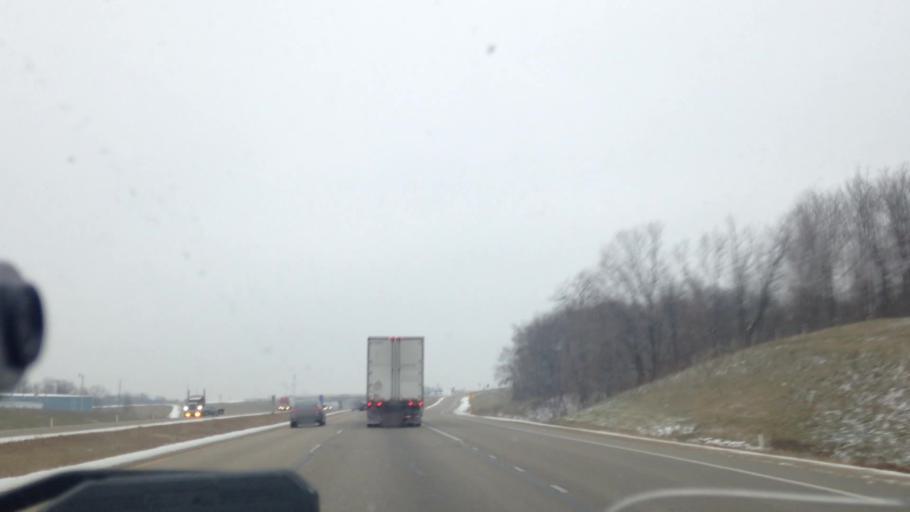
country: US
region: Wisconsin
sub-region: Washington County
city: Slinger
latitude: 43.3519
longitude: -88.2861
